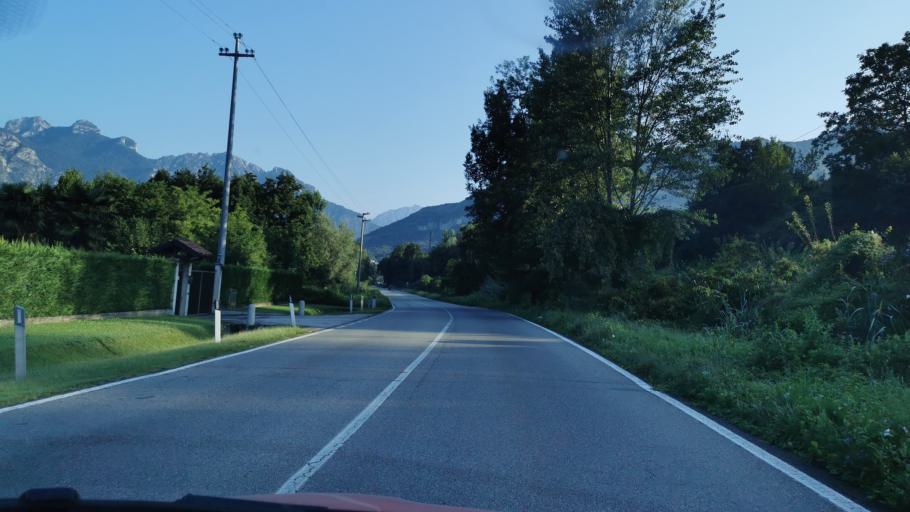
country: IT
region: Lombardy
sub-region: Provincia di Lecco
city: Sala al Barro
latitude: 45.8104
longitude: 9.3600
